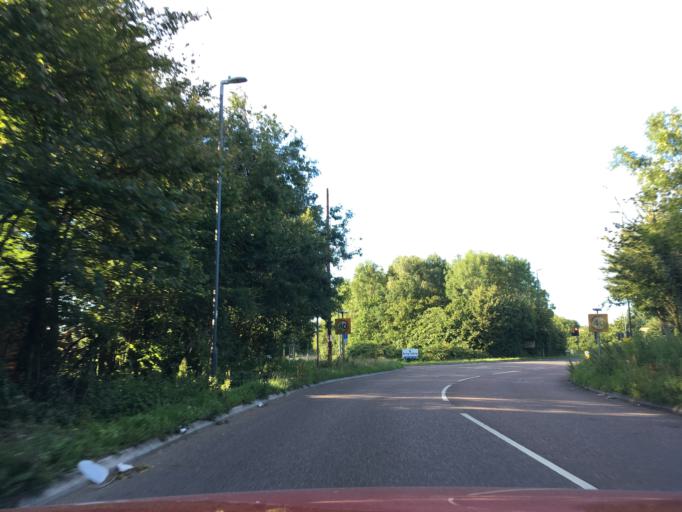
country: GB
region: England
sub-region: South Gloucestershire
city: Siston
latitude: 51.4711
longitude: -2.4789
